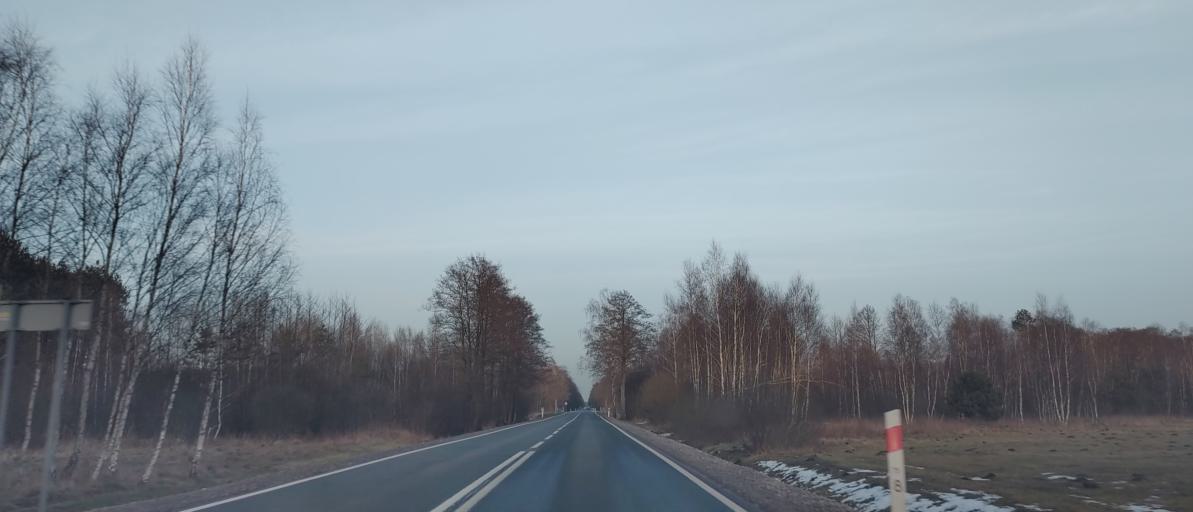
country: PL
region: Masovian Voivodeship
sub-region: Powiat bialobrzeski
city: Sucha
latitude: 51.6323
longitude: 20.8938
